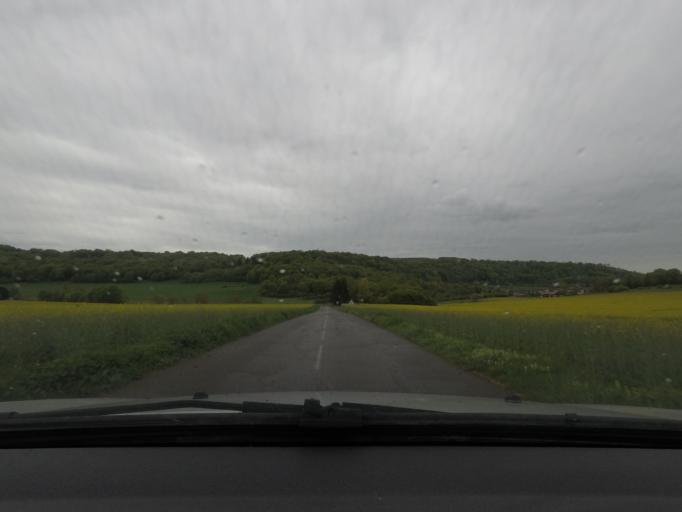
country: BE
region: Wallonia
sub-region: Province du Luxembourg
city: Rouvroy
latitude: 49.4993
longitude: 5.4388
